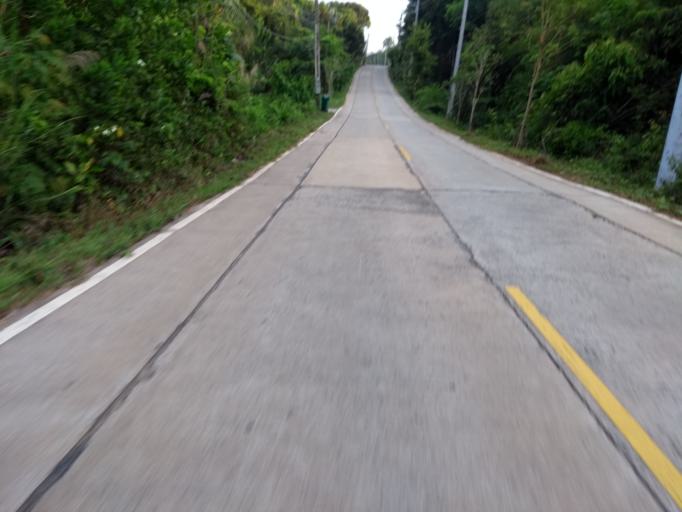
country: TH
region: Trat
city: Ko Kut
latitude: 11.6265
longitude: 102.5467
